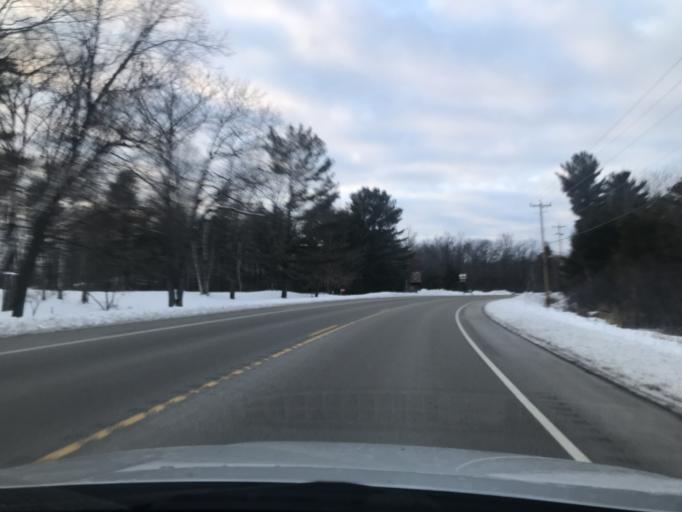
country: US
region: Wisconsin
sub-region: Marinette County
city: Marinette
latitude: 45.1155
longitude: -87.6794
